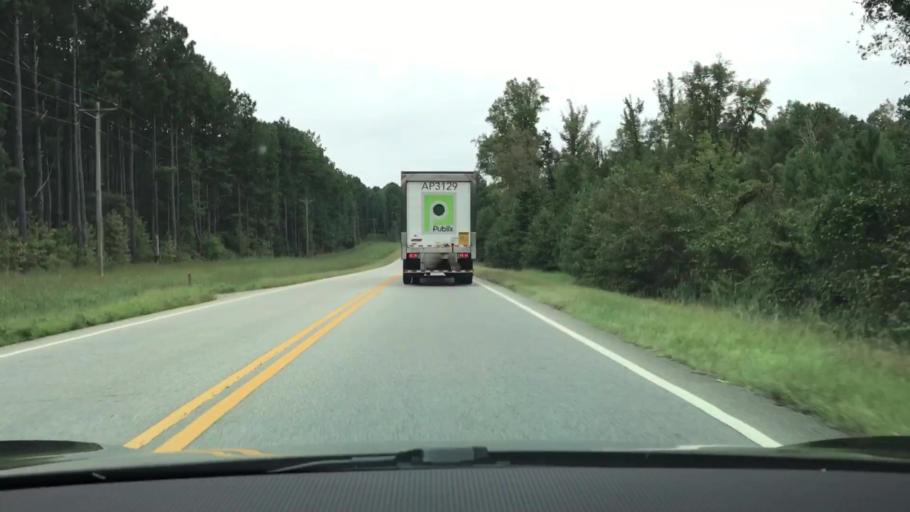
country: US
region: Georgia
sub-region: Greene County
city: Greensboro
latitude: 33.6759
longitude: -83.2676
